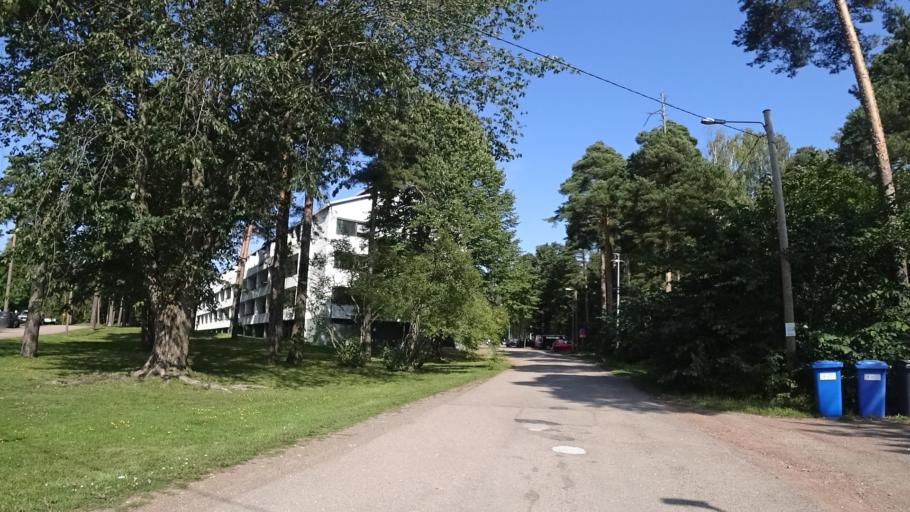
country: FI
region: Kymenlaakso
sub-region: Kotka-Hamina
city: Karhula
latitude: 60.4965
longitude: 26.9590
